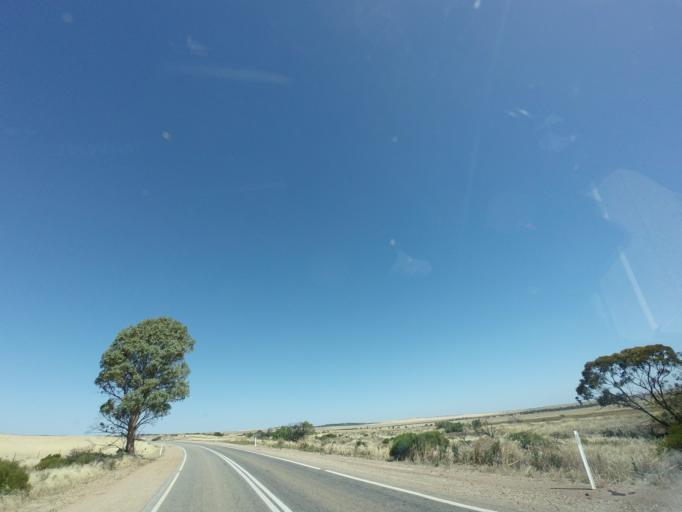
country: AU
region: South Australia
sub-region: Peterborough
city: Peterborough
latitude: -32.9677
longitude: 138.8046
